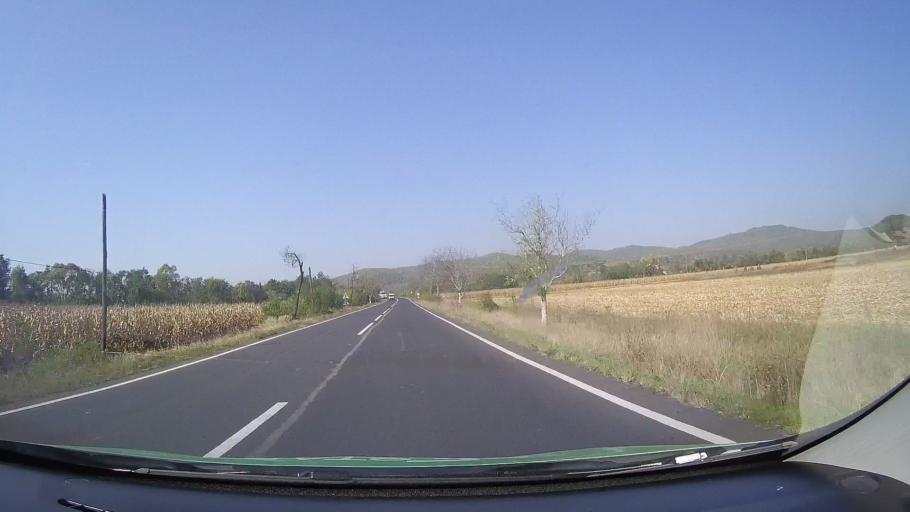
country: RO
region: Hunedoara
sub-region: Comuna Dobra
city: Dobra
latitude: 45.9467
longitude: 22.5998
